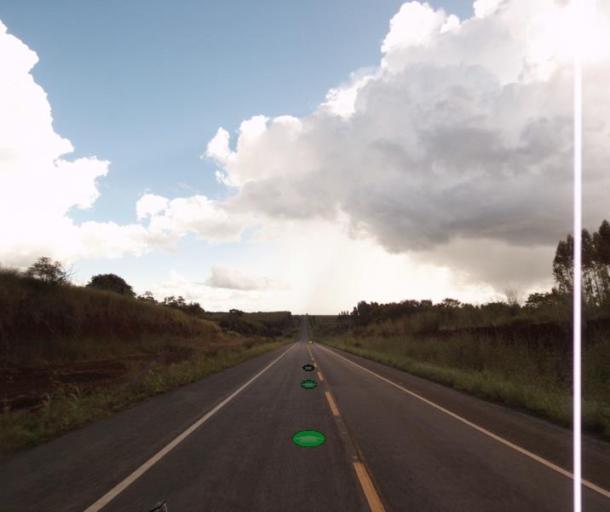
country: BR
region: Goias
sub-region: Itaberai
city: Itaberai
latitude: -15.9867
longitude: -49.7104
